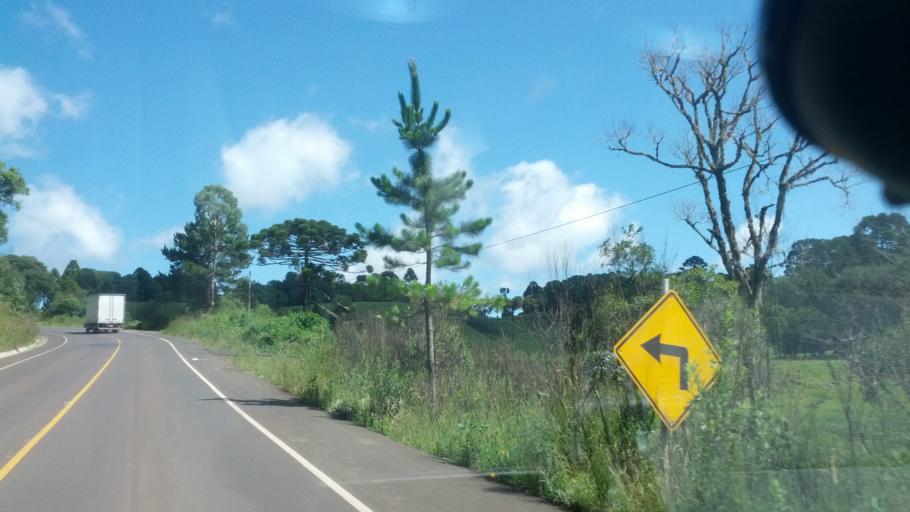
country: BR
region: Santa Catarina
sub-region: Lages
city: Lages
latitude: -27.9254
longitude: -50.5438
